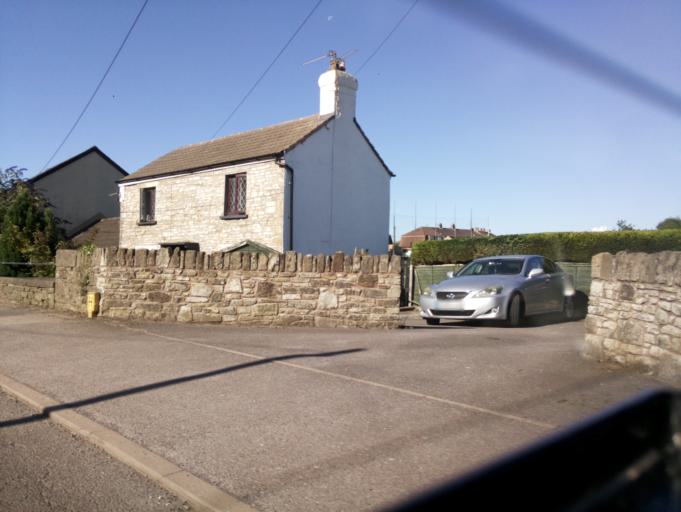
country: GB
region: England
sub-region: Gloucestershire
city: Coleford
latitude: 51.7950
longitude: -2.5984
